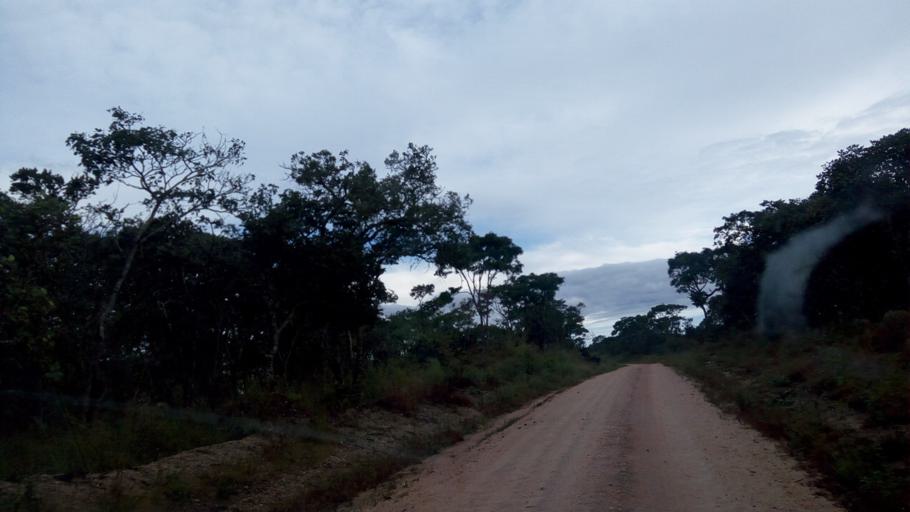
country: CD
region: Katanga
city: Kalemie
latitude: -6.5952
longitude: 29.0406
